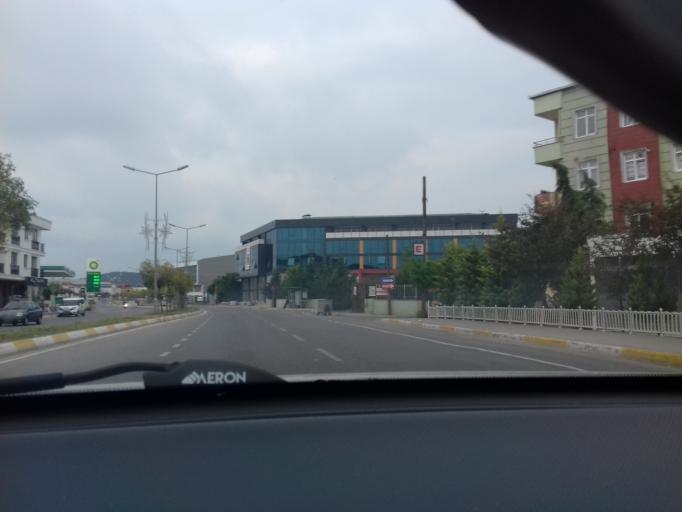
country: TR
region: Istanbul
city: Icmeler
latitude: 40.8948
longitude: 29.3552
